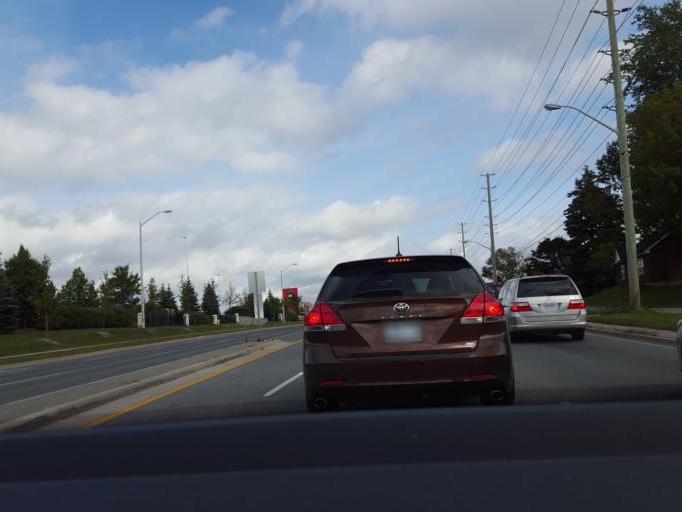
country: CA
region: Ontario
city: Ajax
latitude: 43.9141
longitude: -78.9625
